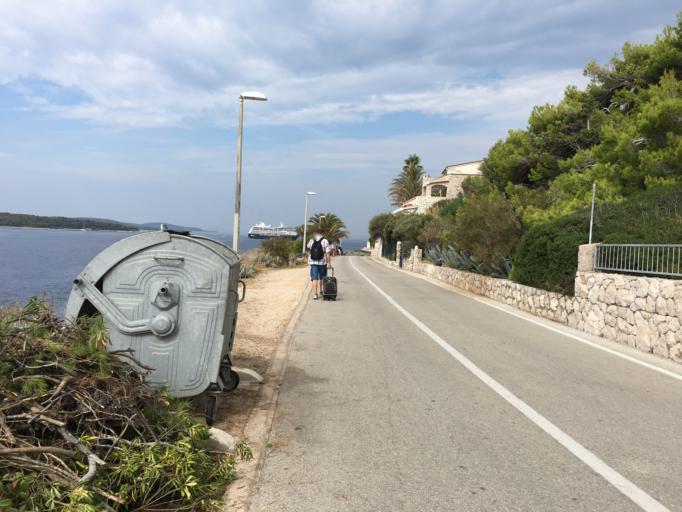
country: HR
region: Splitsko-Dalmatinska
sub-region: Grad Hvar
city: Hvar
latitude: 43.1636
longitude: 16.4435
